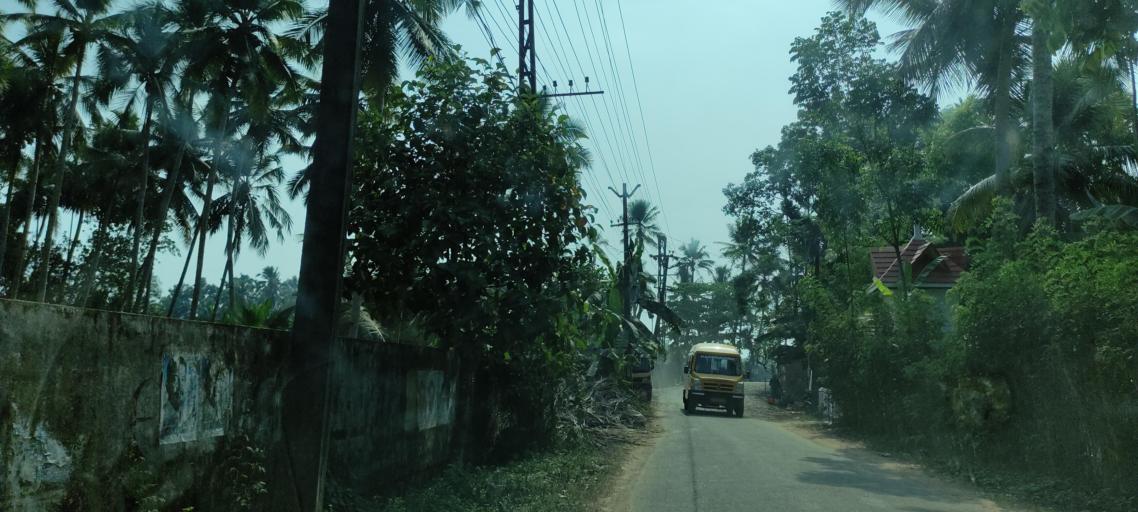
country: IN
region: Kerala
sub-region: Pattanamtitta
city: Tiruvalla
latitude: 9.3612
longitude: 76.5023
